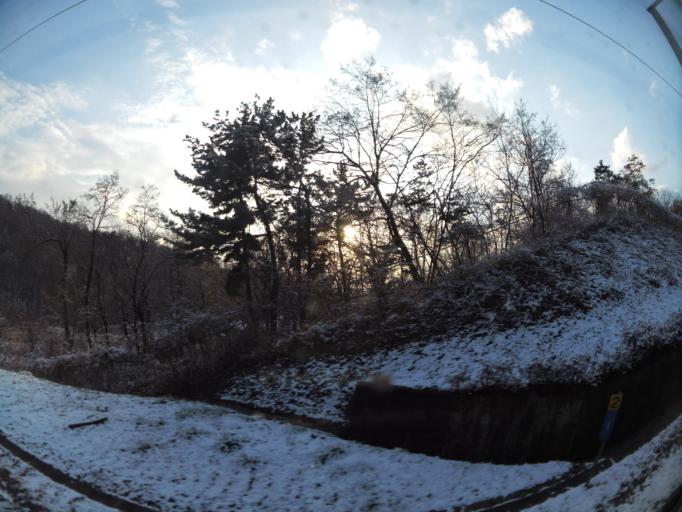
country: KR
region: Daejeon
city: Songgang-dong
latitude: 36.3829
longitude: 127.4158
